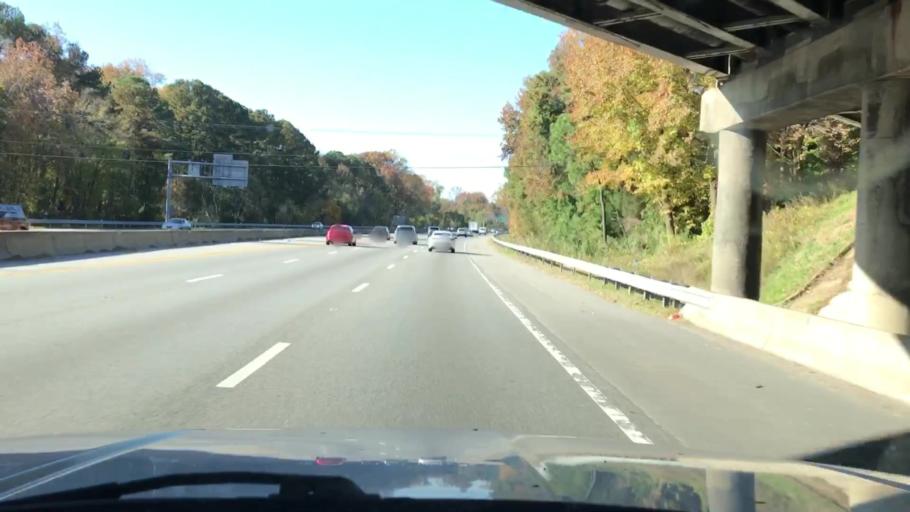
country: US
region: Virginia
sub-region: Henrico County
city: Tuckahoe
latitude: 37.6128
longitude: -77.5380
